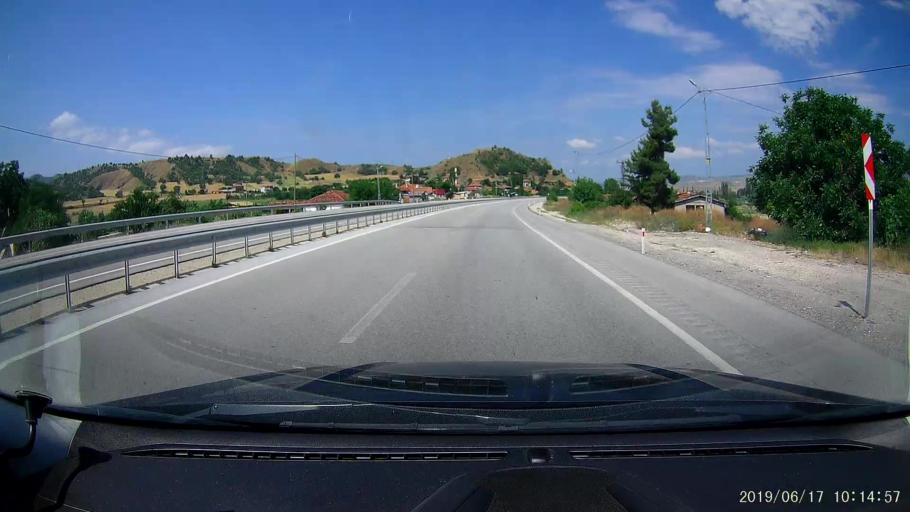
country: TR
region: Amasya
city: Saraycik
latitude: 40.9925
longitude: 35.0147
